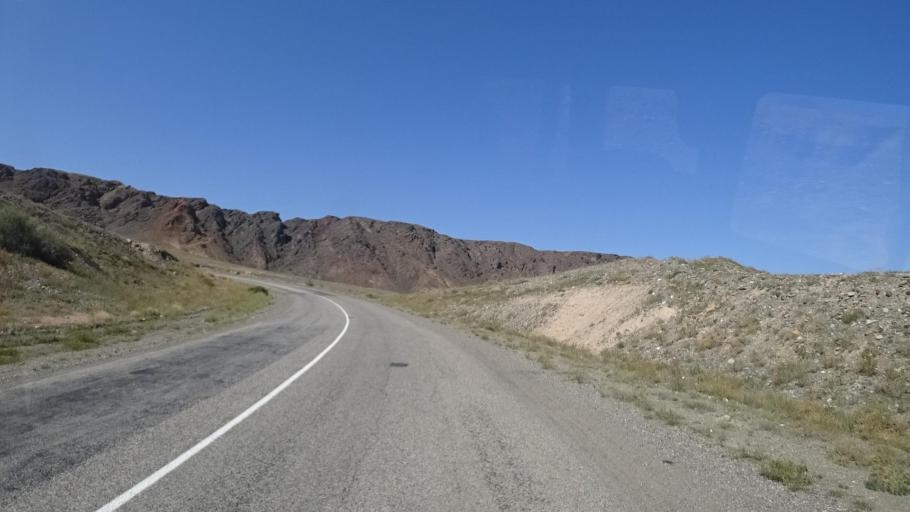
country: KZ
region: Almaty Oblysy
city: Kegen
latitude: 43.2706
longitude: 78.9725
